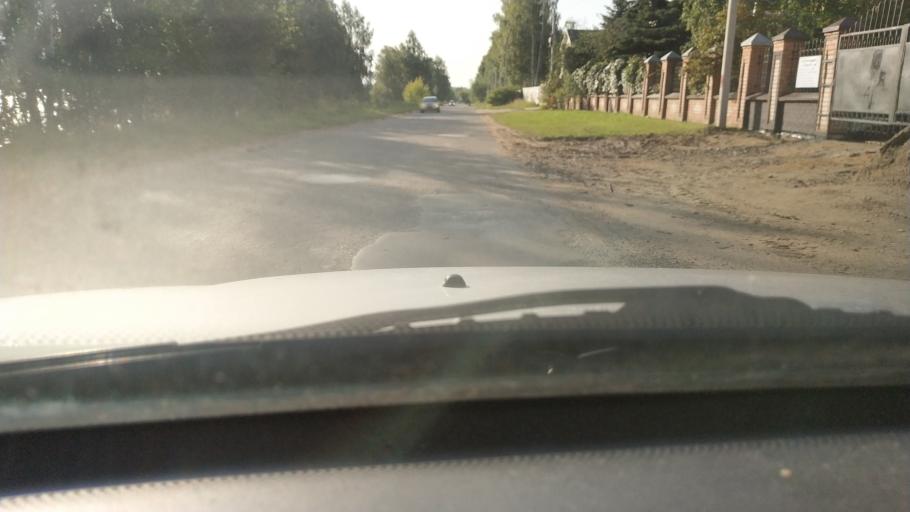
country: RU
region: Kostroma
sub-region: Kostromskoy Rayon
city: Kostroma
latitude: 57.7548
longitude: 40.9195
